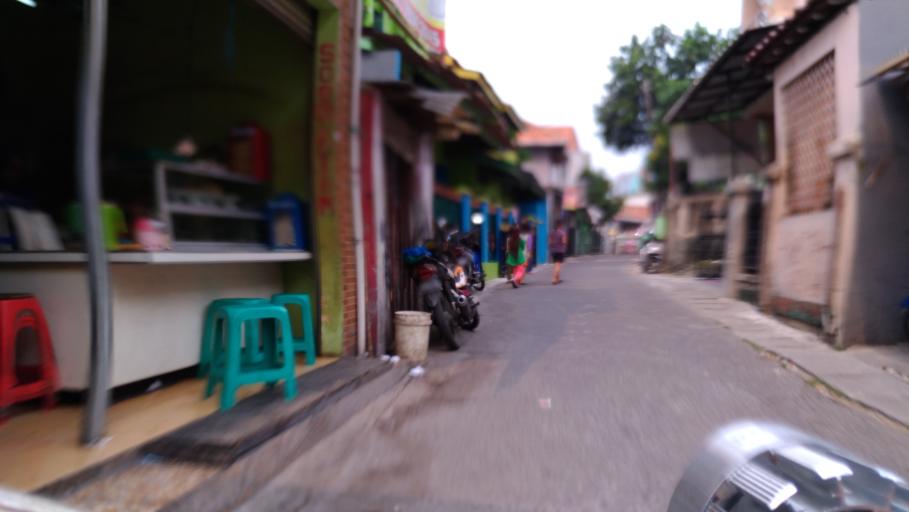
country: ID
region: West Java
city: Depok
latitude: -6.3638
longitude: 106.8568
